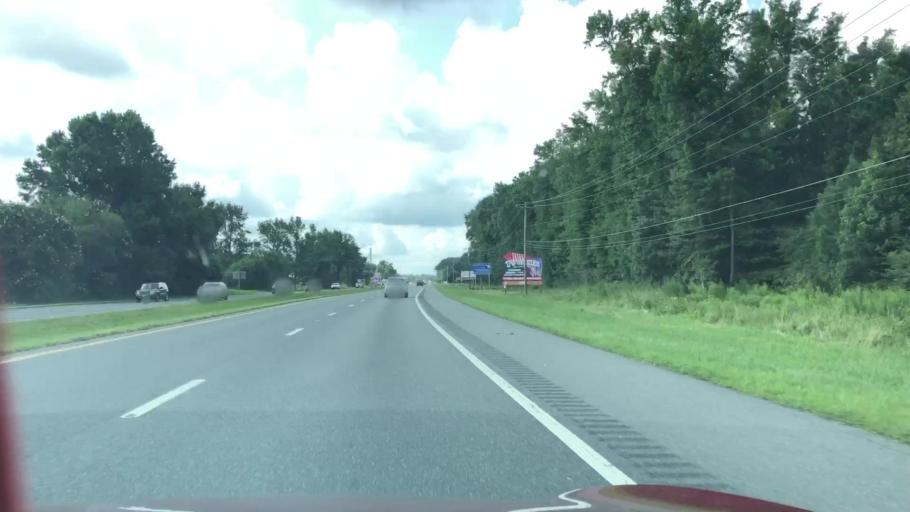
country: US
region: Virginia
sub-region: Accomack County
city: Wattsville
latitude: 37.9574
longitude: -75.5343
